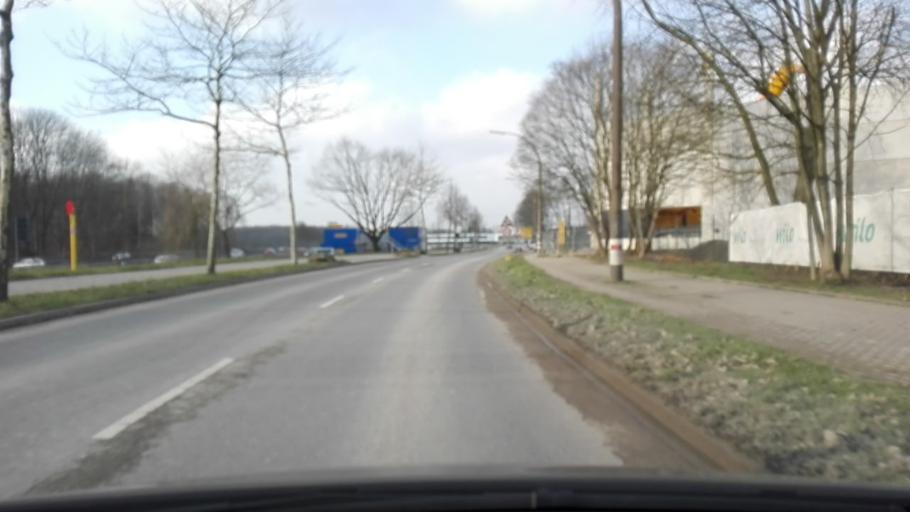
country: DE
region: North Rhine-Westphalia
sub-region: Regierungsbezirk Arnsberg
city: Dortmund
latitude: 51.4821
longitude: 7.4773
